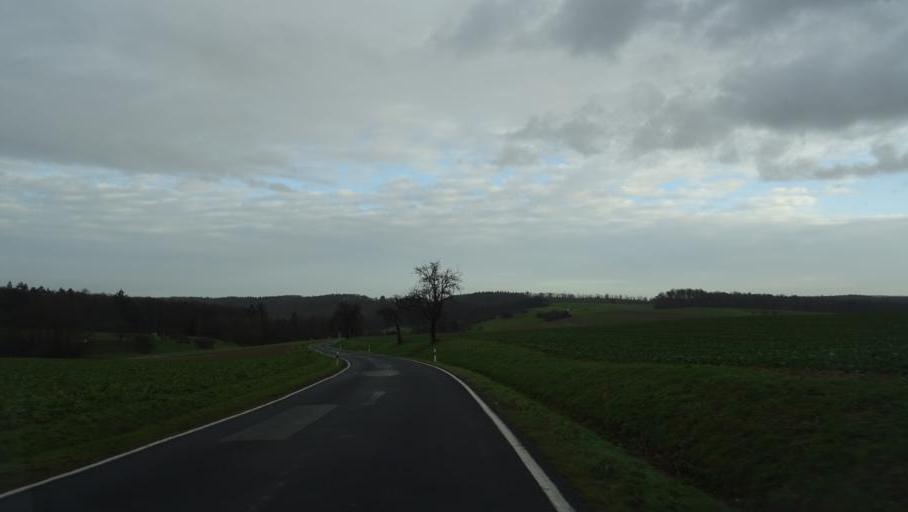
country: DE
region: Baden-Wuerttemberg
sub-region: Karlsruhe Region
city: Neunkirchen
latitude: 49.3845
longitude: 9.0222
